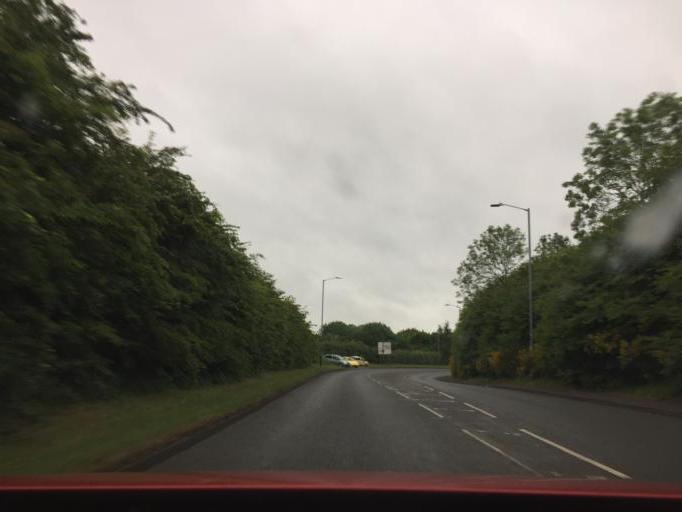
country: GB
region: England
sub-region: Warwickshire
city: Attleborough
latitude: 52.5164
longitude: -1.4450
